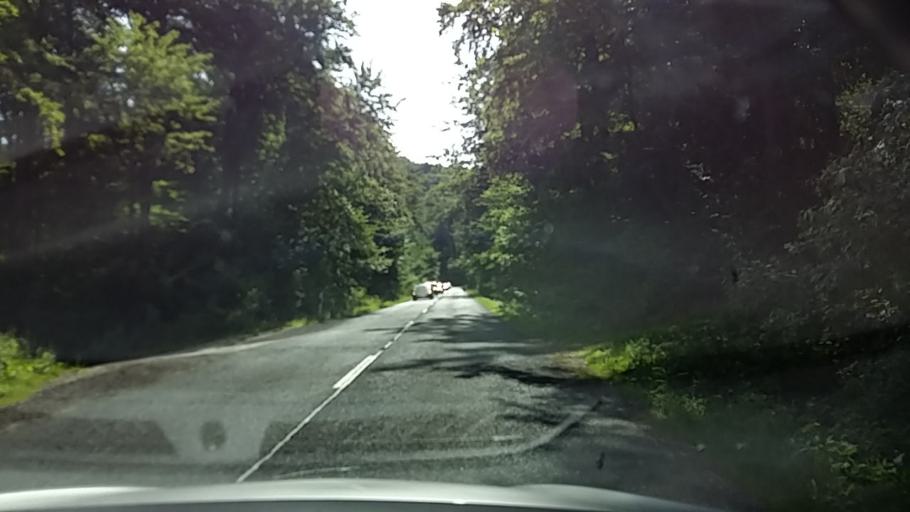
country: HU
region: Pest
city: Pilisszentkereszt
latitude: 47.7189
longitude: 18.8612
